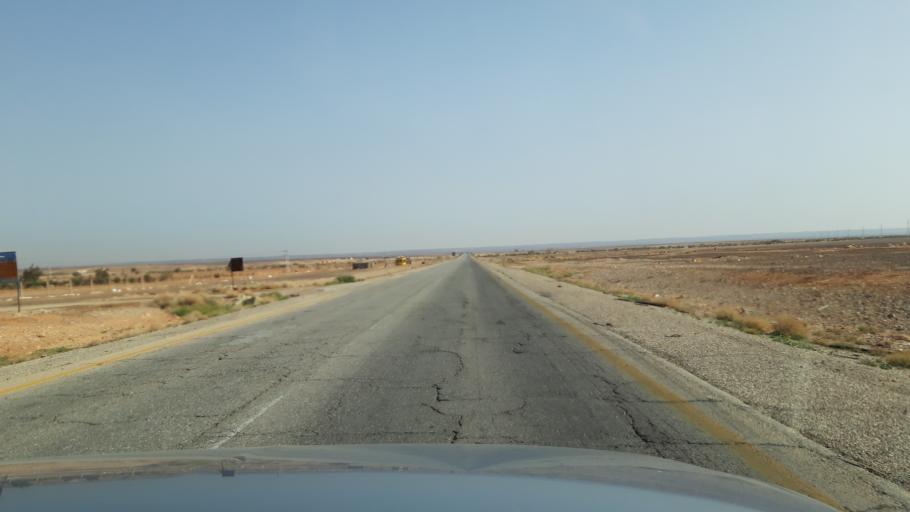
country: JO
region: Amman
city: Al Azraq ash Shamali
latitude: 31.7927
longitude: 36.5839
